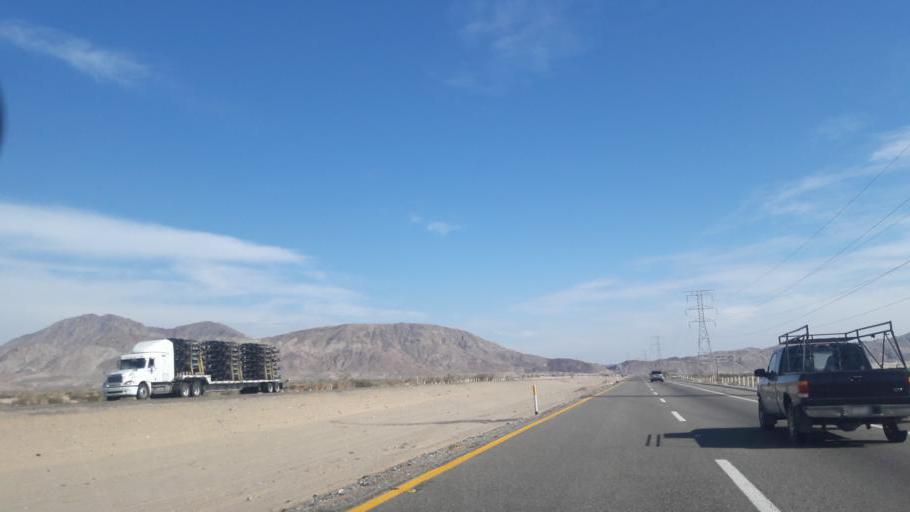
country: MX
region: Baja California
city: Progreso
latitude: 32.5743
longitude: -115.7655
